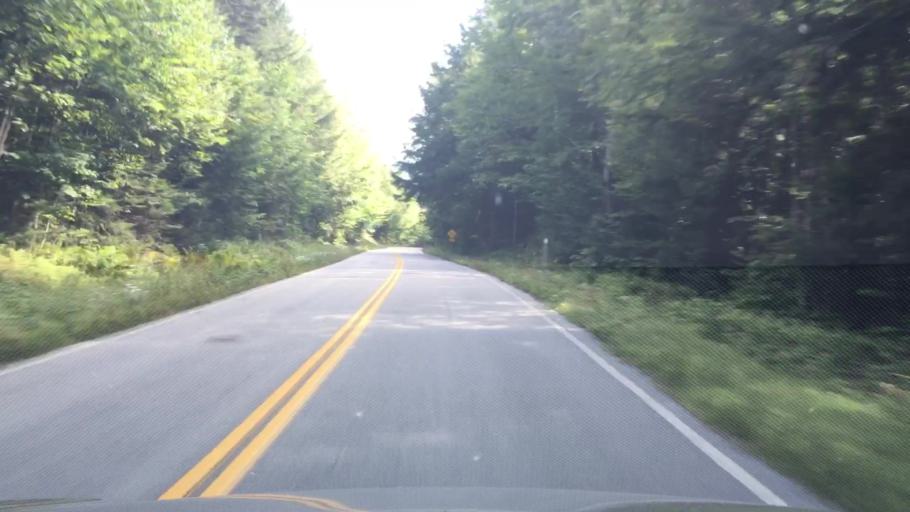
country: US
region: New Hampshire
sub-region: Carroll County
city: Tamworth
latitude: 44.0101
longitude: -71.3211
